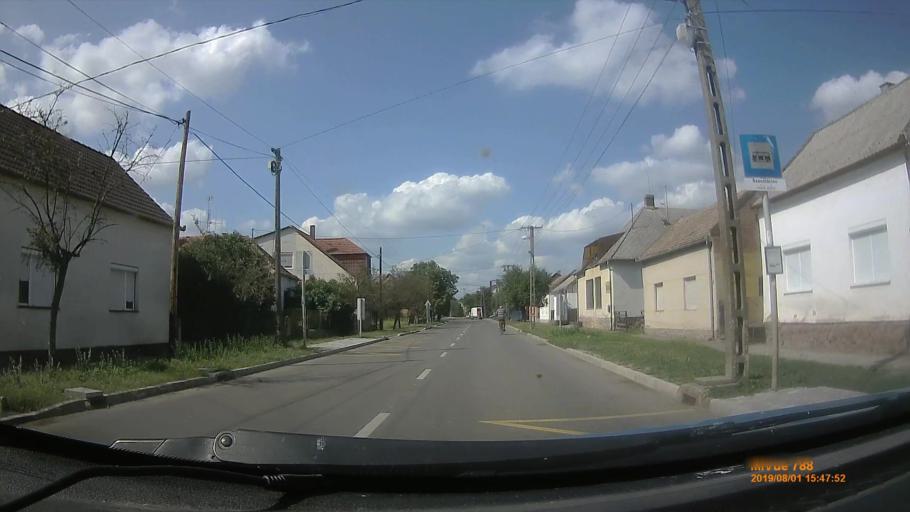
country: HU
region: Baranya
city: Szentlorinc
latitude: 46.0342
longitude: 17.9849
